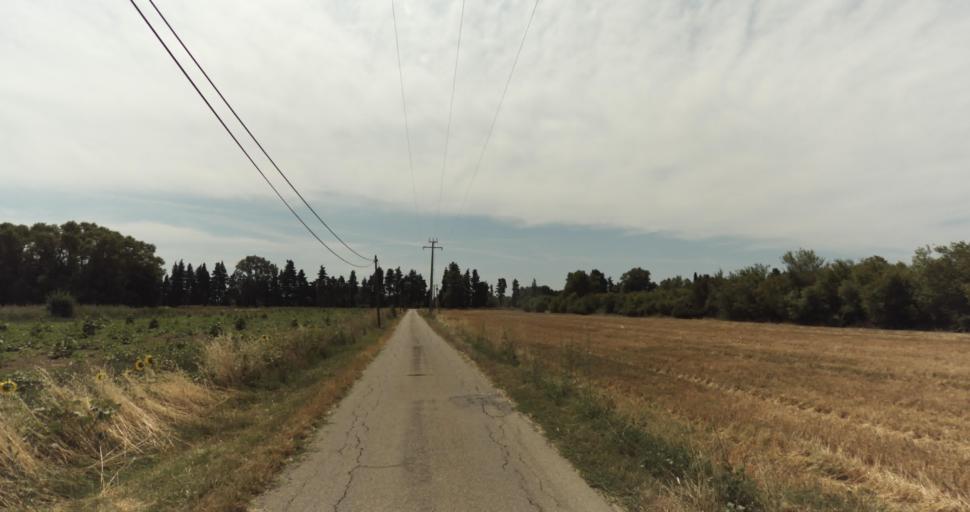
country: FR
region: Provence-Alpes-Cote d'Azur
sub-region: Departement du Vaucluse
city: Althen-des-Paluds
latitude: 44.0298
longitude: 4.9538
